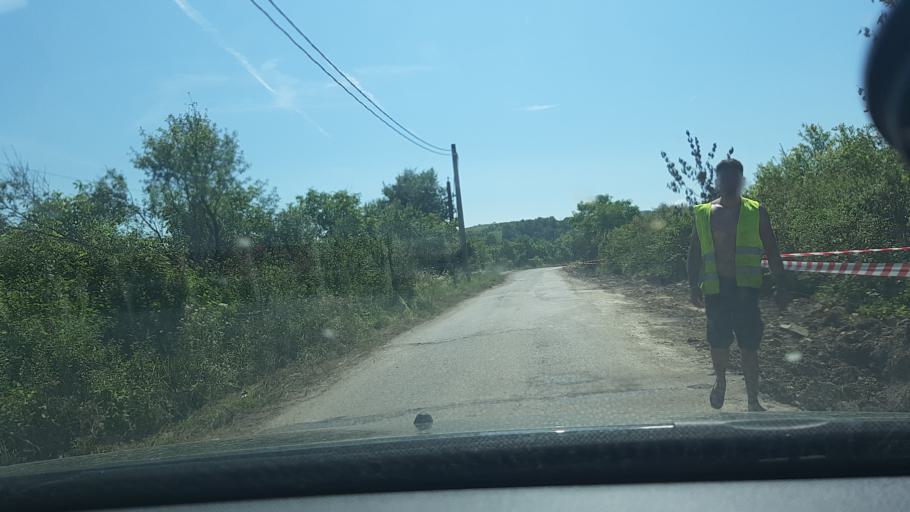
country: RO
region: Hunedoara
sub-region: Comuna Teliucu Inferior
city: Teliucu Inferior
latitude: 45.6893
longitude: 22.8679
